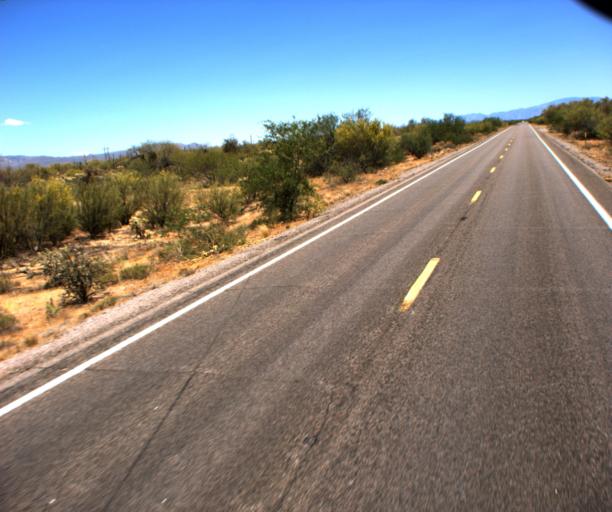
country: US
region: Arizona
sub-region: Pima County
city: Marana
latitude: 32.7645
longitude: -111.1512
